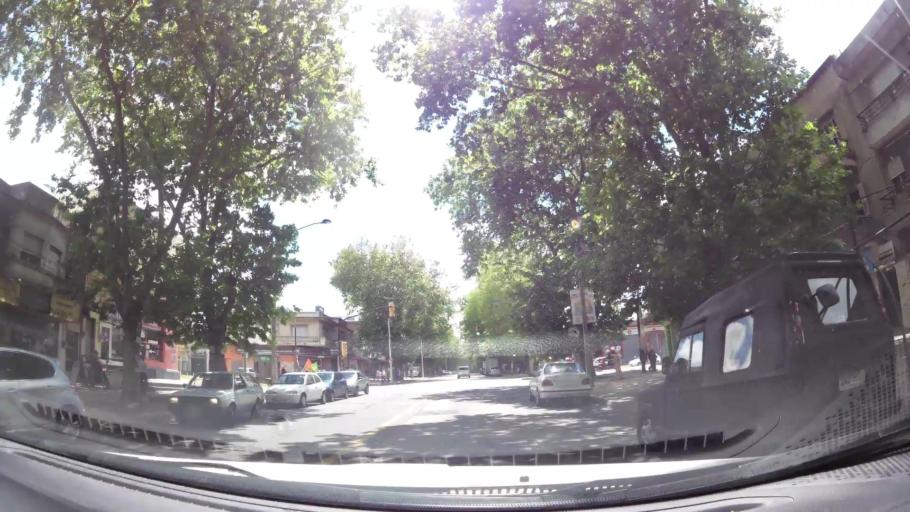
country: UY
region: Montevideo
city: Montevideo
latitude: -34.8581
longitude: -56.2263
